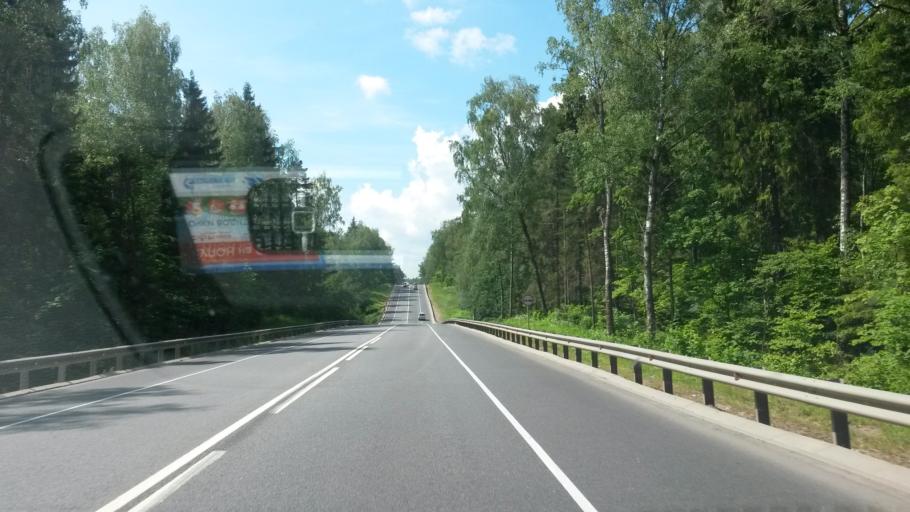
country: RU
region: Jaroslavl
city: Pereslavl'-Zalesskiy
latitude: 56.8602
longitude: 38.9488
